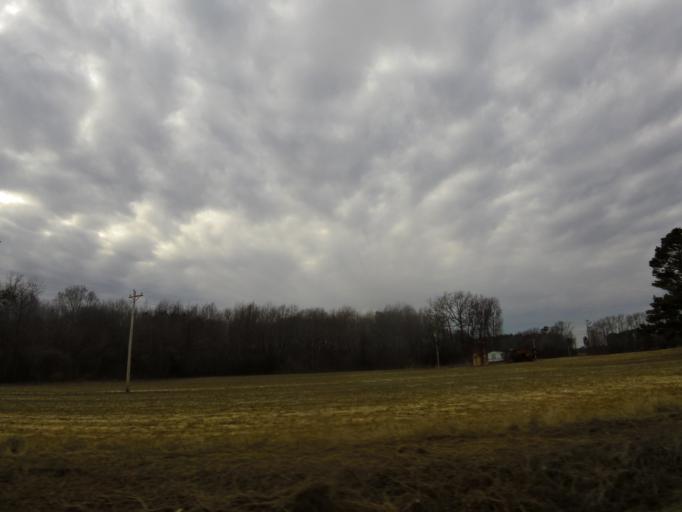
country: US
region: North Carolina
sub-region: Hertford County
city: Murfreesboro
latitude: 36.3802
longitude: -77.1604
